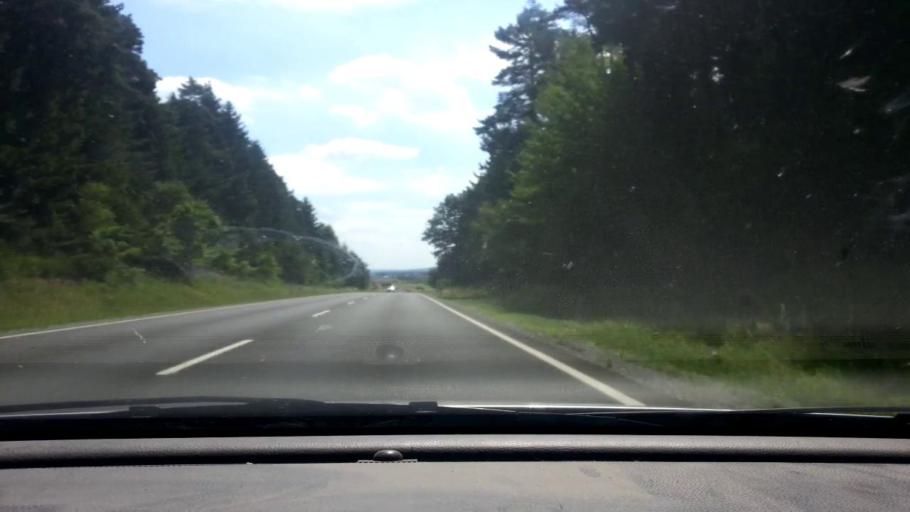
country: DE
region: Bavaria
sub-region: Upper Franconia
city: Seybothenreuth
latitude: 49.8833
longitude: 11.7448
